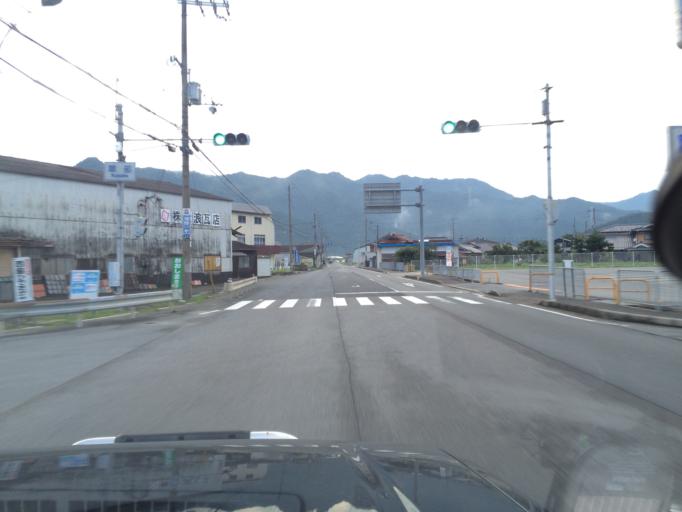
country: JP
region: Hyogo
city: Nishiwaki
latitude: 35.1010
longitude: 134.9962
